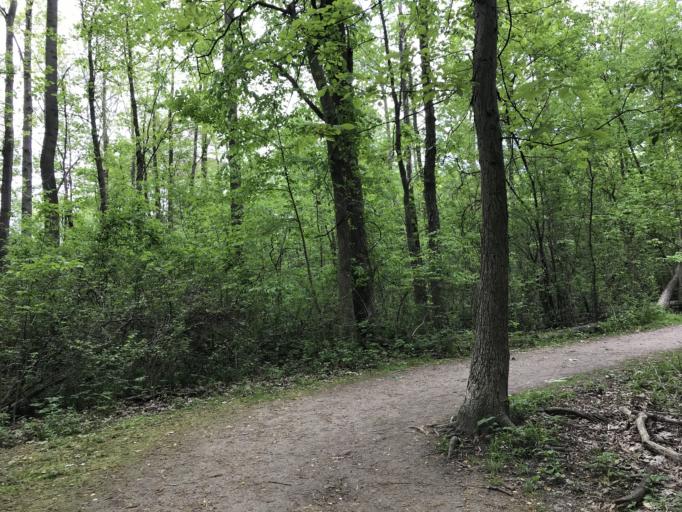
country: US
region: Michigan
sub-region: Oakland County
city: Franklin
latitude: 42.4680
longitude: -83.3144
